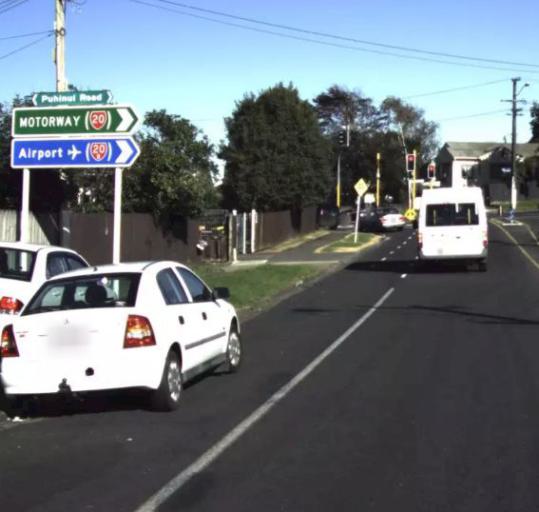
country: NZ
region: Auckland
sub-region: Auckland
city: Wiri
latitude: -36.9912
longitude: 174.8476
